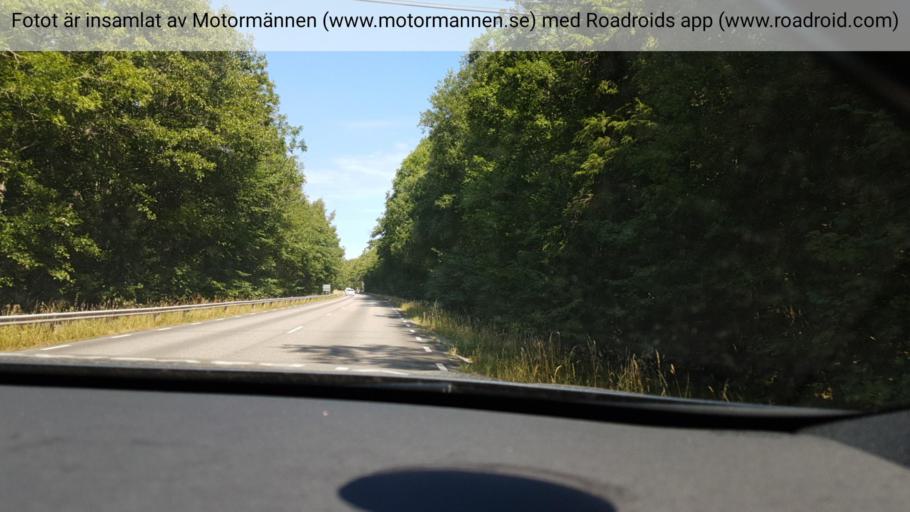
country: SE
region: Vaestra Goetaland
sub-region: Gotene Kommun
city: Kallby
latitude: 58.6039
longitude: 13.3969
